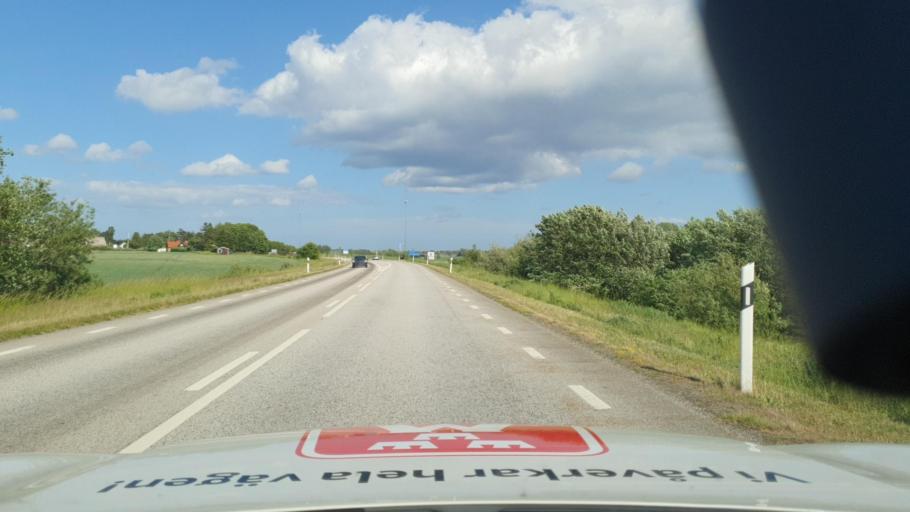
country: SE
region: Skane
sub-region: Simrishamns Kommun
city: Simrishamn
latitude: 55.5351
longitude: 14.2724
